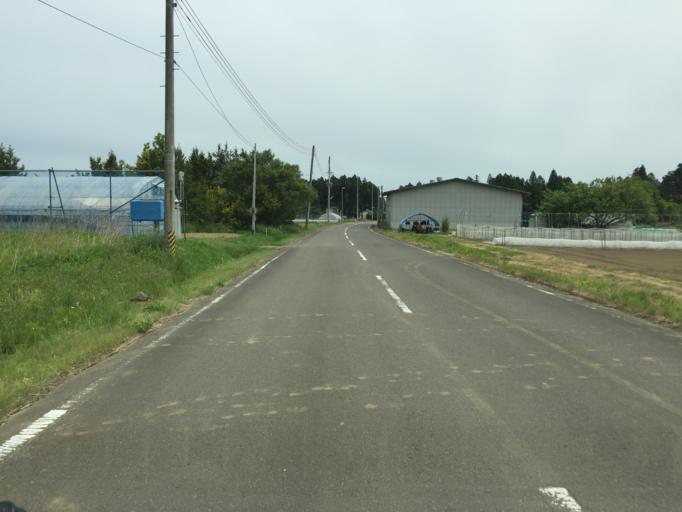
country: JP
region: Fukushima
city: Fukushima-shi
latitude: 37.7142
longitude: 140.3759
